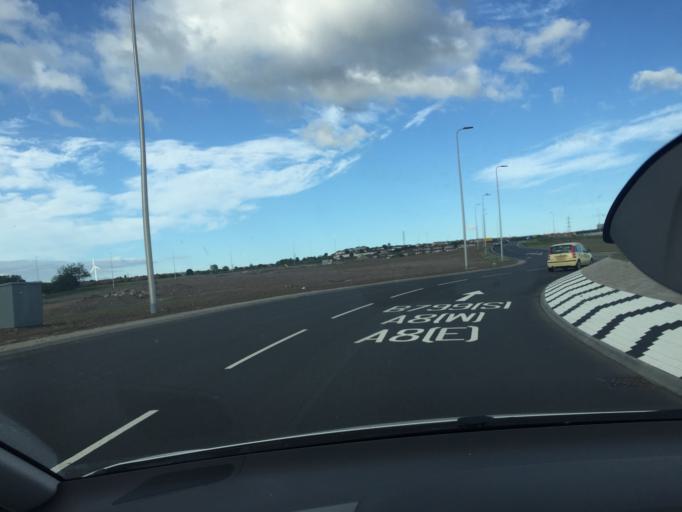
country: GB
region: Scotland
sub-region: North Lanarkshire
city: Chapelhall
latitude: 55.8353
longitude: -3.9636
